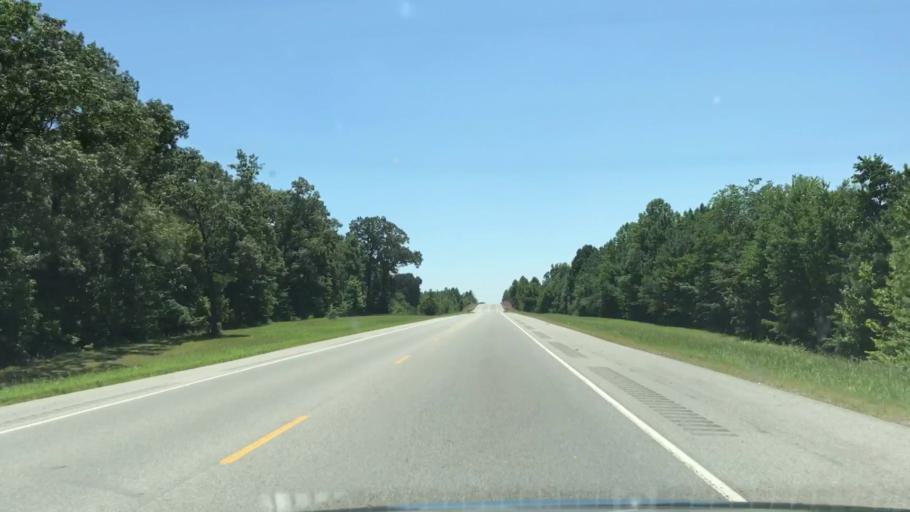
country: US
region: Tennessee
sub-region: Putnam County
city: Baxter
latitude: 36.1654
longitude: -85.6280
